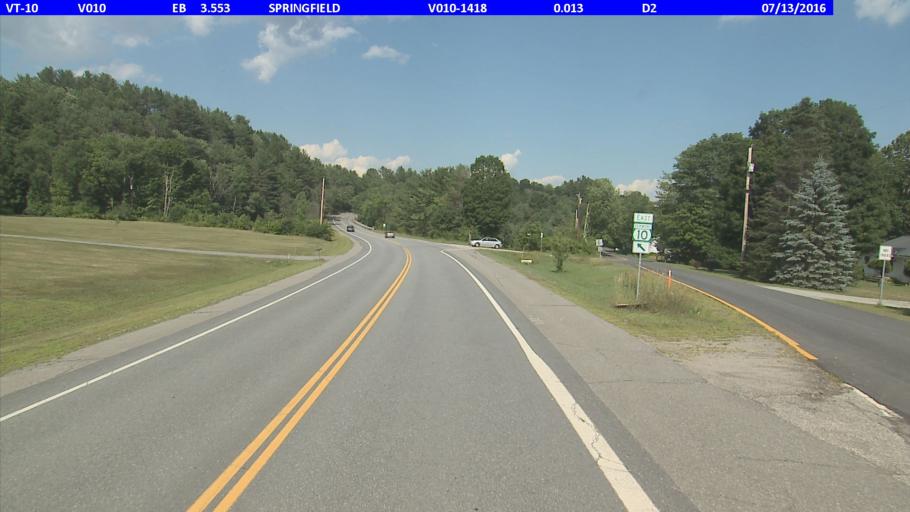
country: US
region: Vermont
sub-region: Windsor County
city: Springfield
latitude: 43.3350
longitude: -72.5462
